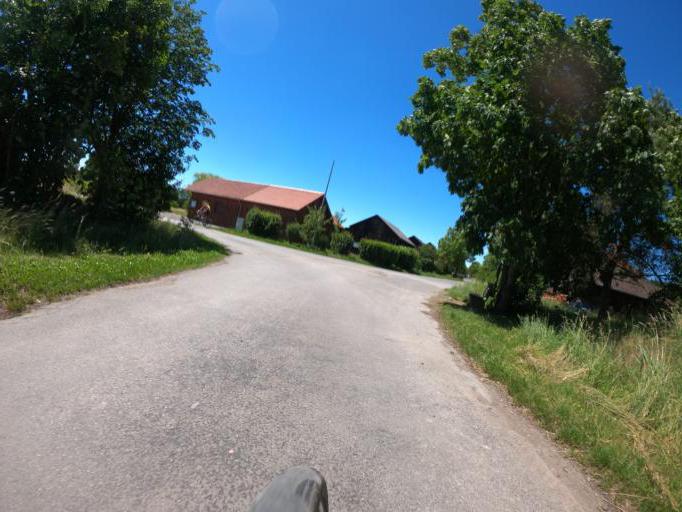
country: DE
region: Baden-Wuerttemberg
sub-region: Regierungsbezirk Stuttgart
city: Sersheim
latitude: 48.9802
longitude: 8.9953
